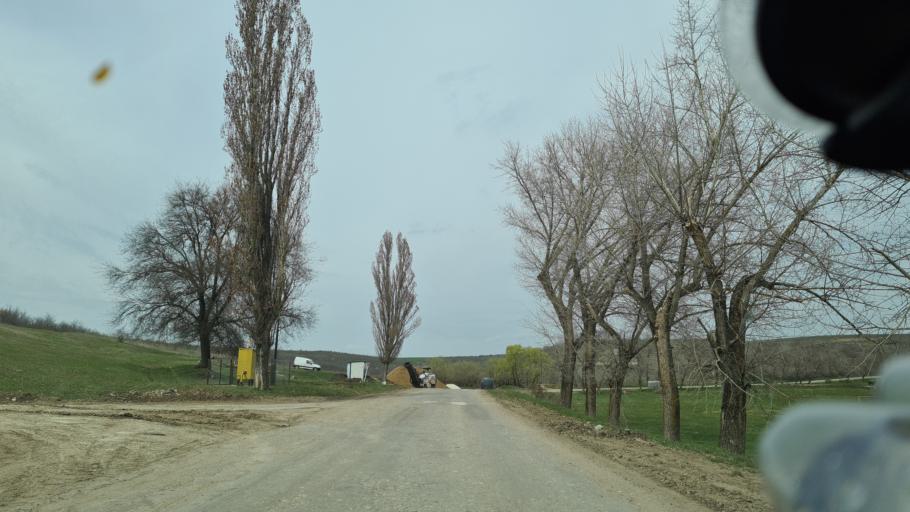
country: MD
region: Chisinau
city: Singera
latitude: 46.8401
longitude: 28.9794
